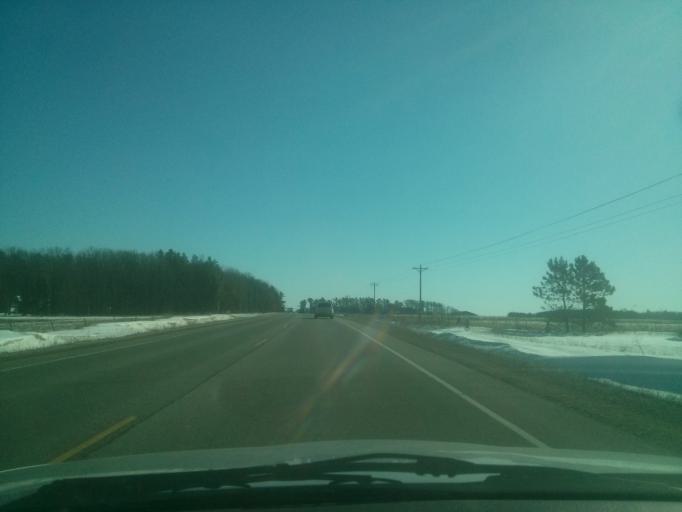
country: US
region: Wisconsin
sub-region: Saint Croix County
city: New Richmond
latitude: 45.1367
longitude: -92.4074
